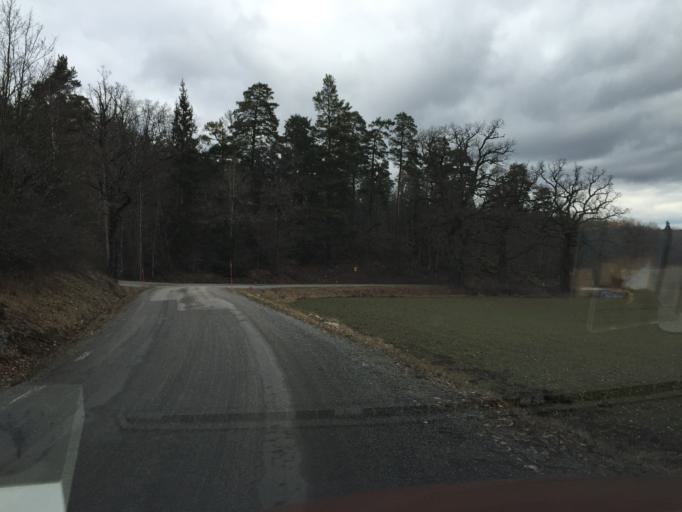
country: SE
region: Stockholm
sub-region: Salems Kommun
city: Ronninge
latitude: 59.2506
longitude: 17.6919
